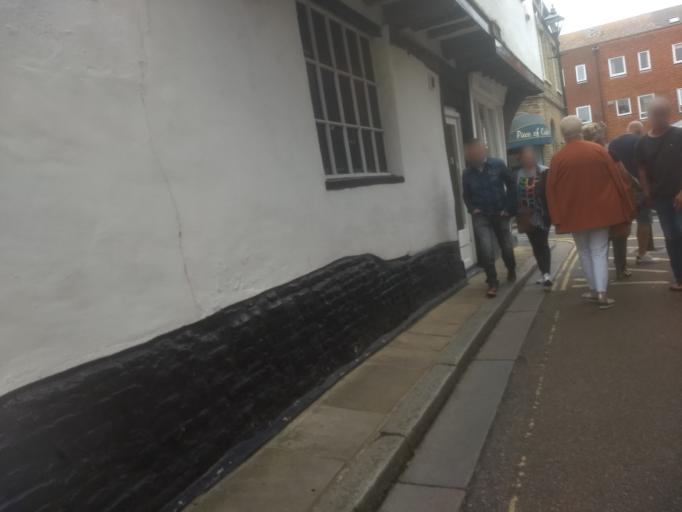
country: GB
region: England
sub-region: Kent
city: Sandwich
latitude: 51.2760
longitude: 1.3404
